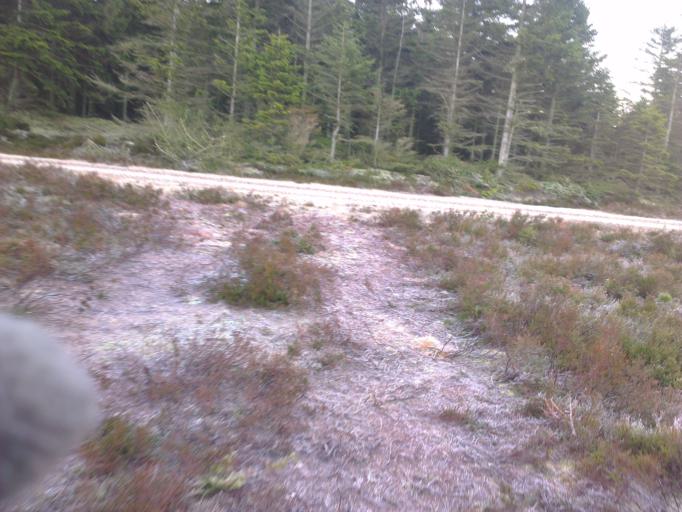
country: DK
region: Central Jutland
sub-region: Holstebro Kommune
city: Ulfborg
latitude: 56.2512
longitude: 8.4223
